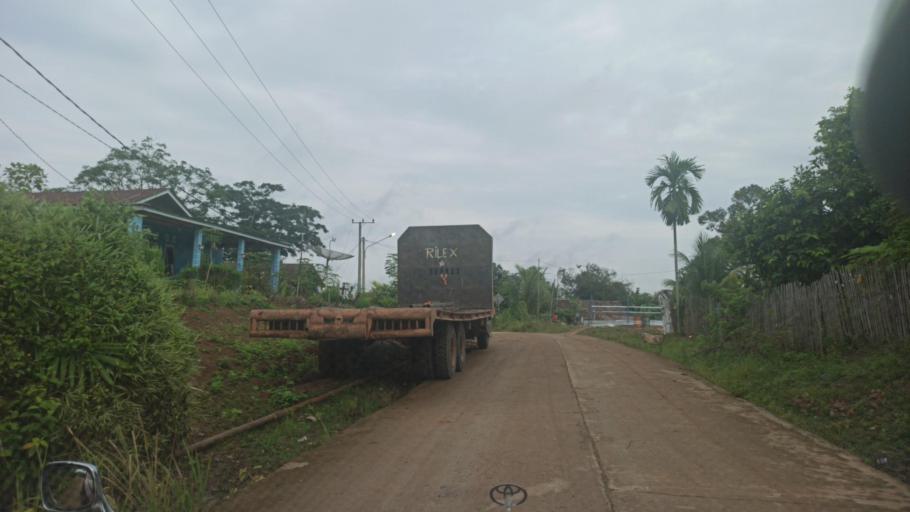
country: ID
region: South Sumatra
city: Gunungmegang Dalam
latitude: -3.2885
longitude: 103.6679
